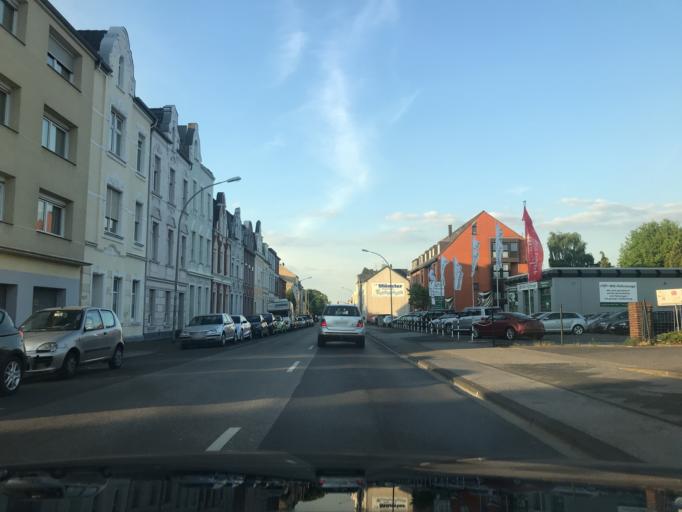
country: DE
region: North Rhine-Westphalia
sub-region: Regierungsbezirk Dusseldorf
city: Monchengladbach
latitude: 51.1850
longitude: 6.4139
